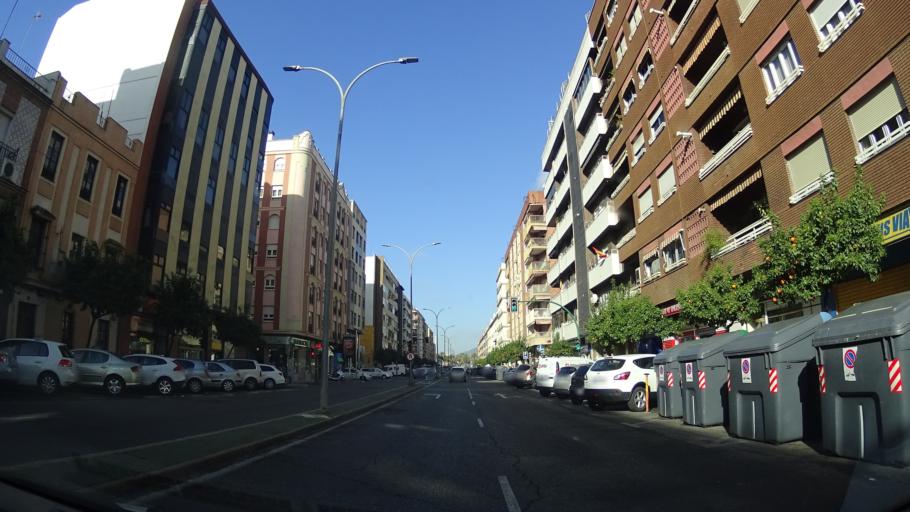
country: ES
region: Andalusia
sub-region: Province of Cordoba
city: Cordoba
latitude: 37.8852
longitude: -4.7905
